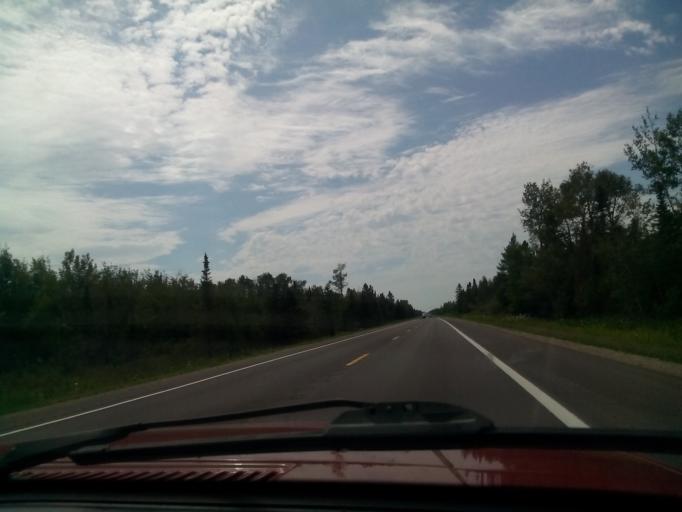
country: US
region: Michigan
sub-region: Schoolcraft County
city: Manistique
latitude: 46.0445
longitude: -85.9702
